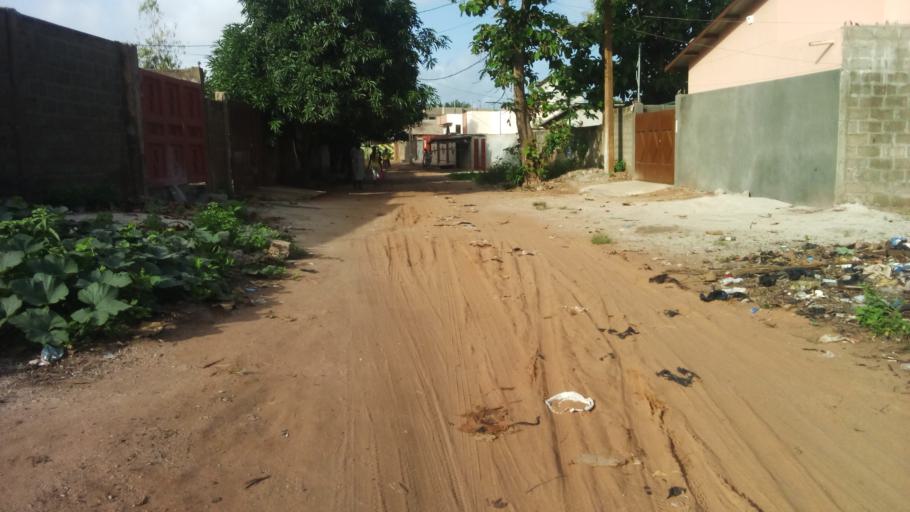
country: BJ
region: Atlantique
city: Abomey-Calavi
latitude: 6.4341
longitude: 2.3423
